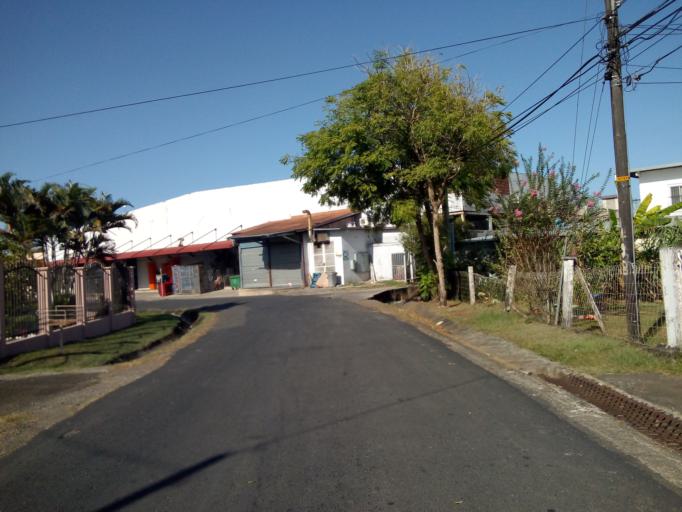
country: PA
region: Veraguas
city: Santiago de Veraguas
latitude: 8.1050
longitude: -80.9712
